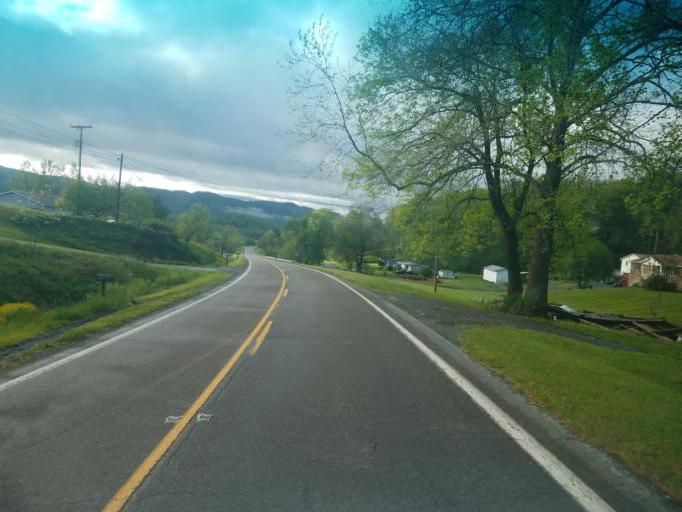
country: US
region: Virginia
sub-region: Washington County
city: Emory
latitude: 36.6801
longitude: -81.8141
